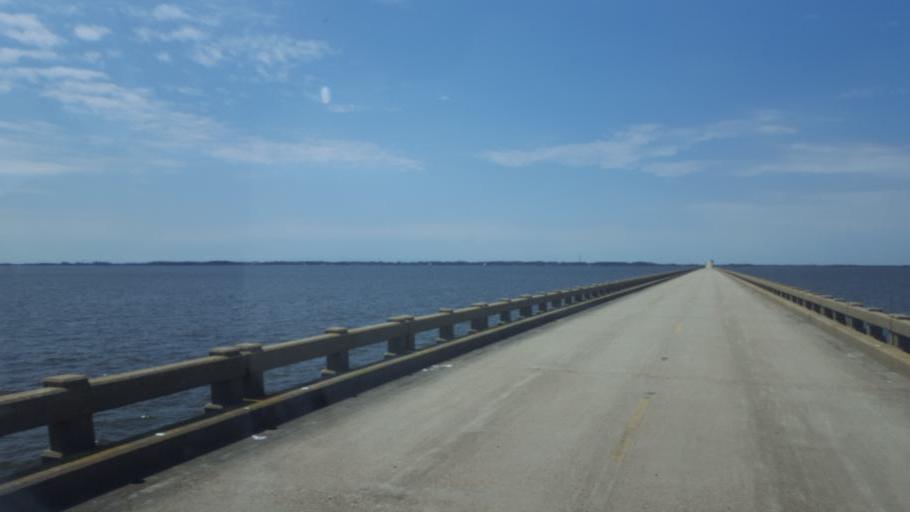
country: US
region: North Carolina
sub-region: Dare County
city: Manteo
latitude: 35.9236
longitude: -75.7343
